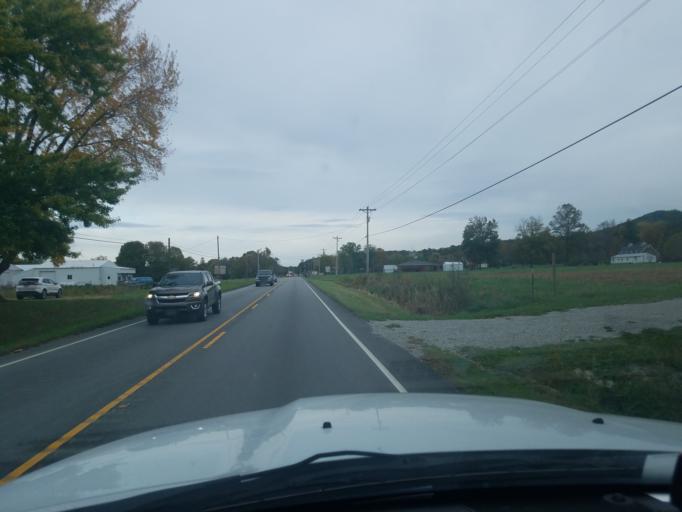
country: US
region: Indiana
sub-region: Clark County
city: Sellersburg
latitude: 38.4440
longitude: -85.8524
